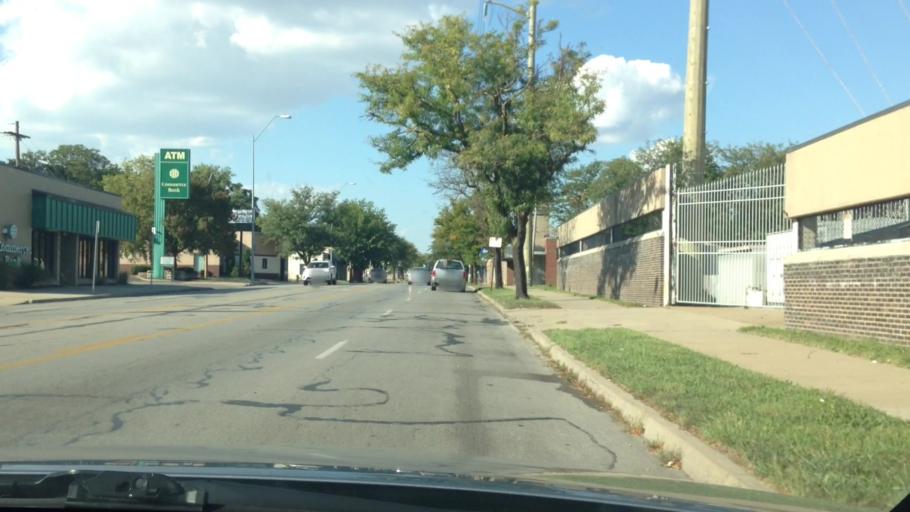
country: US
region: Kansas
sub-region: Johnson County
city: Mission Hills
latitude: 39.0159
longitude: -94.5744
